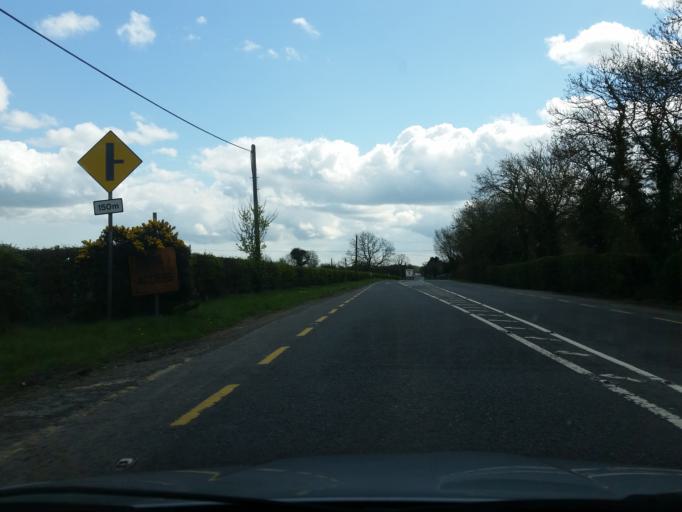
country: IE
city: Kentstown
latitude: 53.6500
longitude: -6.5137
